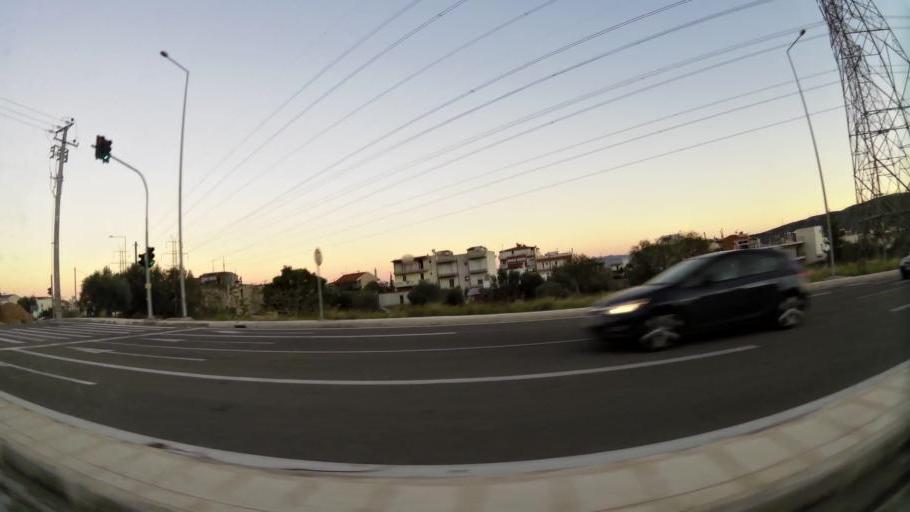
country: GR
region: Attica
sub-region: Nomarchia Dytikis Attikis
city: Ano Liosia
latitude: 38.0872
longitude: 23.6822
